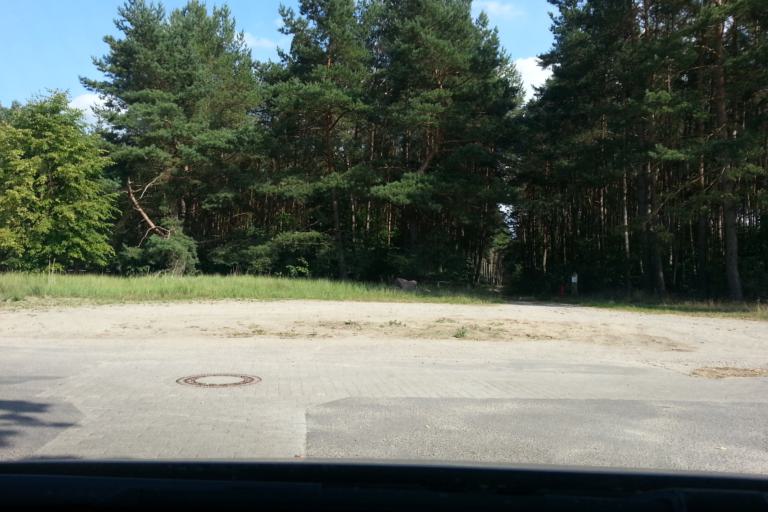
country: DE
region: Mecklenburg-Vorpommern
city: Ferdinandshof
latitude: 53.6289
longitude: 13.8654
